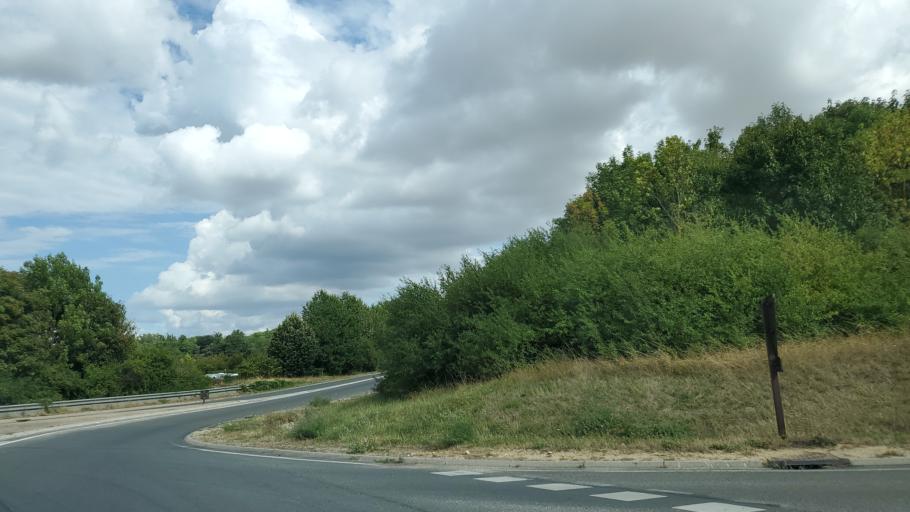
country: FR
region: Ile-de-France
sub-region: Departement de Seine-et-Marne
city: Coulommiers
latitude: 48.7974
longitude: 3.0951
